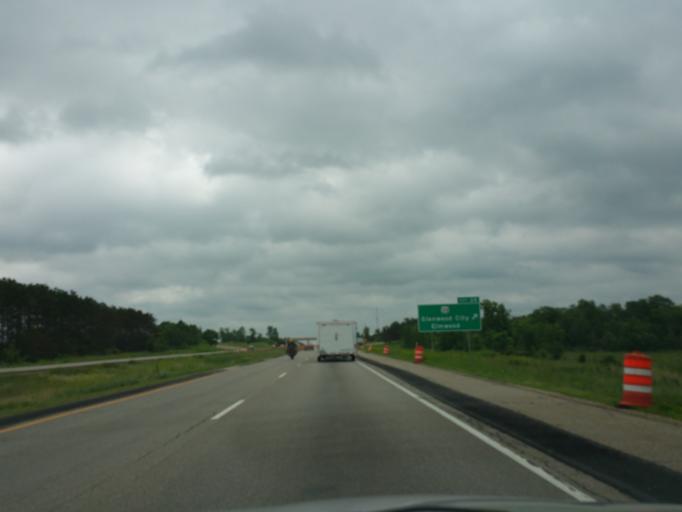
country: US
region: Wisconsin
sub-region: Saint Croix County
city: Woodville
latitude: 44.9334
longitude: -92.2049
